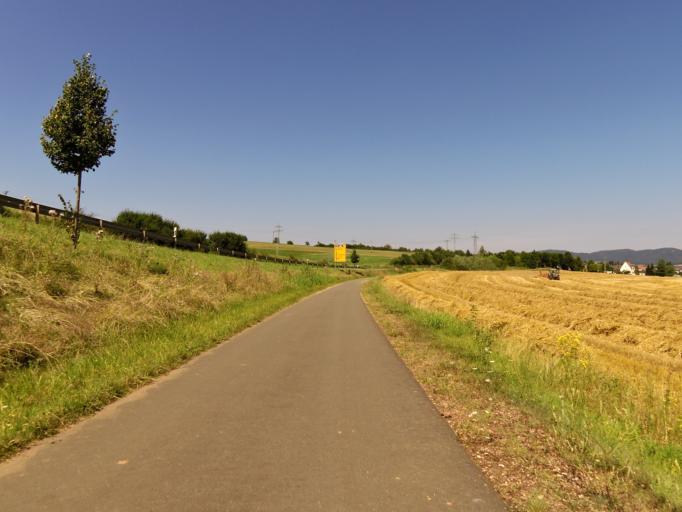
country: DE
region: Rheinland-Pfalz
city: Munchweiler an der Alsenz
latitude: 49.5412
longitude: 7.8812
